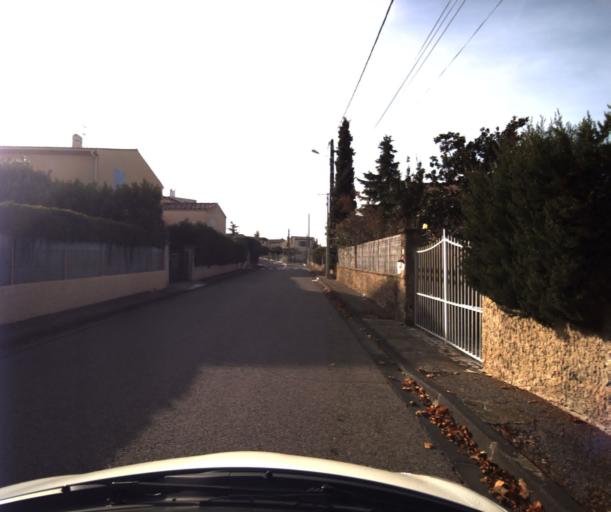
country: FR
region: Provence-Alpes-Cote d'Azur
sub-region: Departement du Vaucluse
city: Pertuis
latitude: 43.6906
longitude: 5.5136
